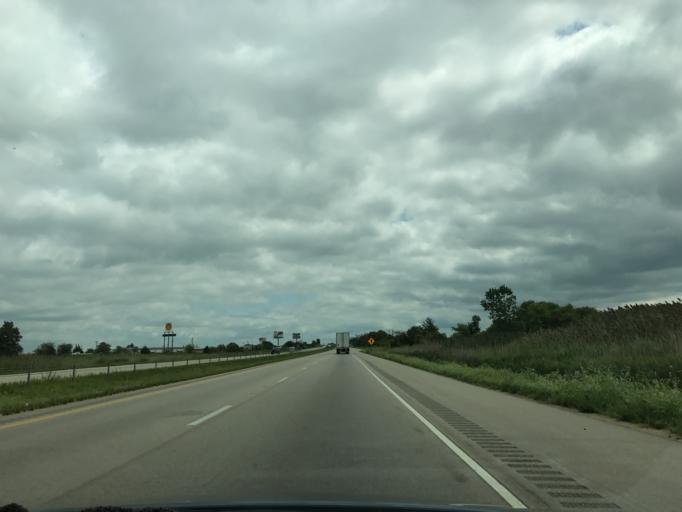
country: US
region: Illinois
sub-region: LaSalle County
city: Ottawa
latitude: 41.3764
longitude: -88.7791
